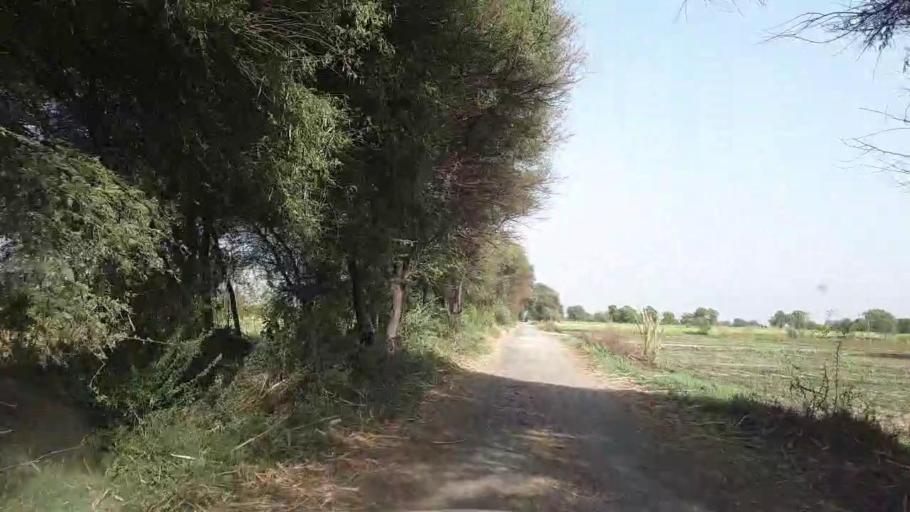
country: PK
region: Sindh
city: Tando Ghulam Ali
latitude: 25.0762
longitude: 68.8392
